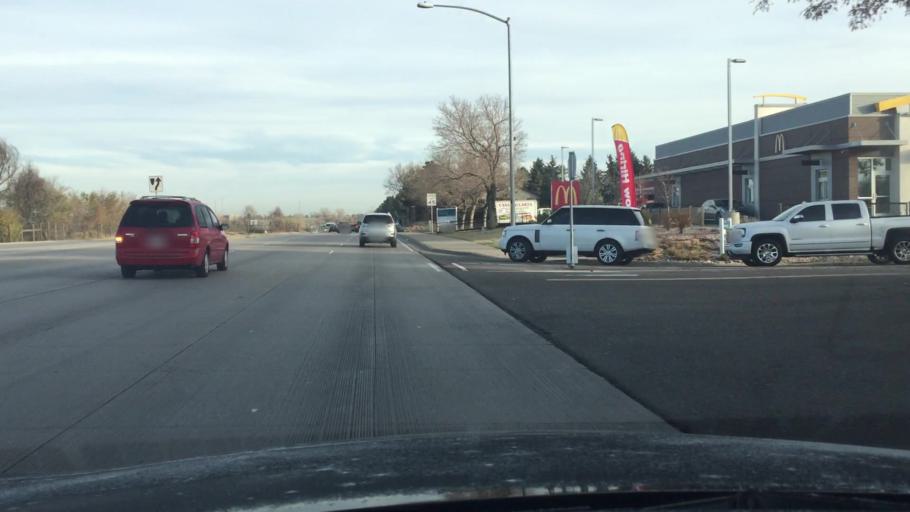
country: US
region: Colorado
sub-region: Arapahoe County
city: Dove Valley
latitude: 39.6414
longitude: -104.8287
